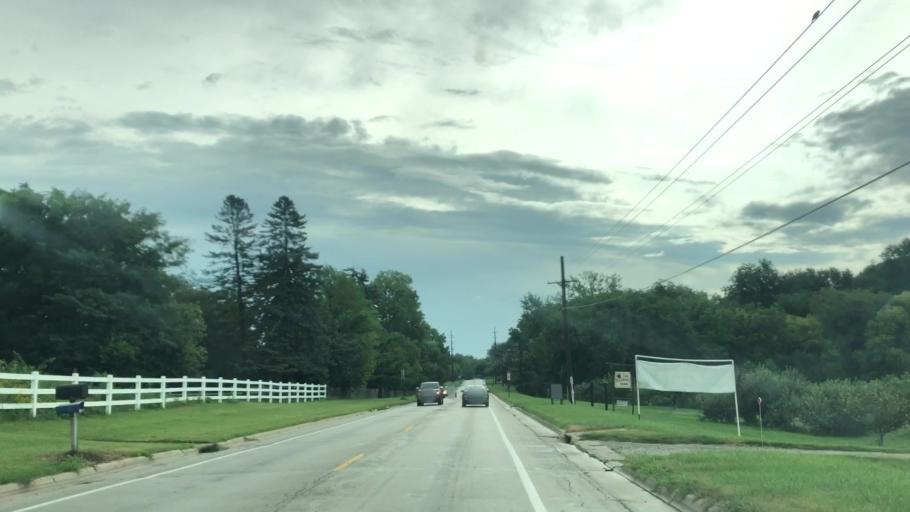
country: US
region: Iowa
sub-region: Marshall County
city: Marshalltown
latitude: 42.0490
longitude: -92.9507
